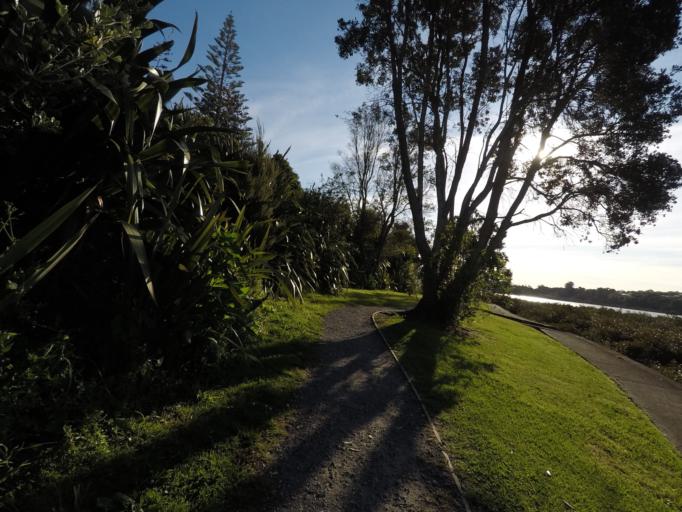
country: NZ
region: Auckland
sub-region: Auckland
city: Rosebank
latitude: -36.8246
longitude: 174.6469
